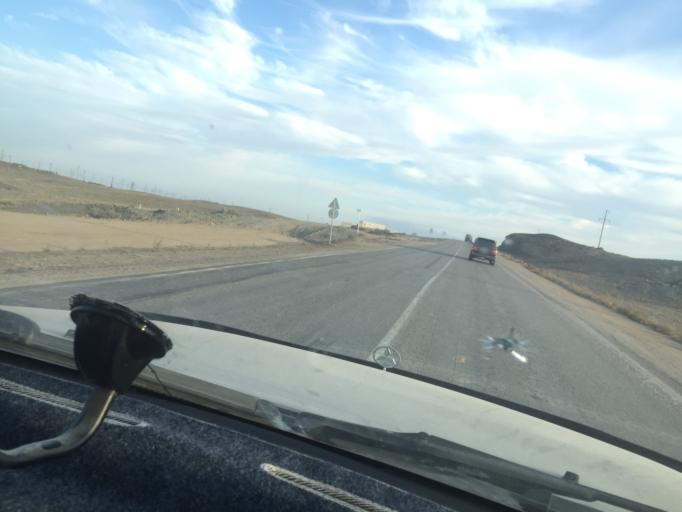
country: KZ
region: Almaty Oblysy
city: Ulken
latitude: 45.2058
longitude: 73.8849
